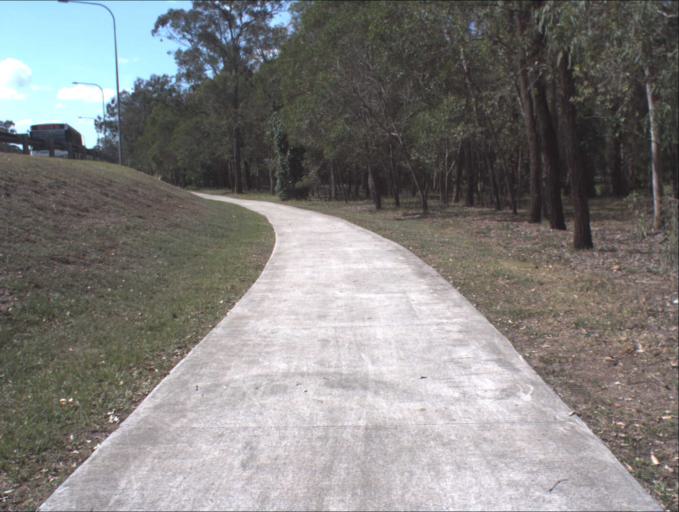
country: AU
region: Queensland
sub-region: Logan
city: Slacks Creek
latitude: -27.6538
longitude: 153.1459
